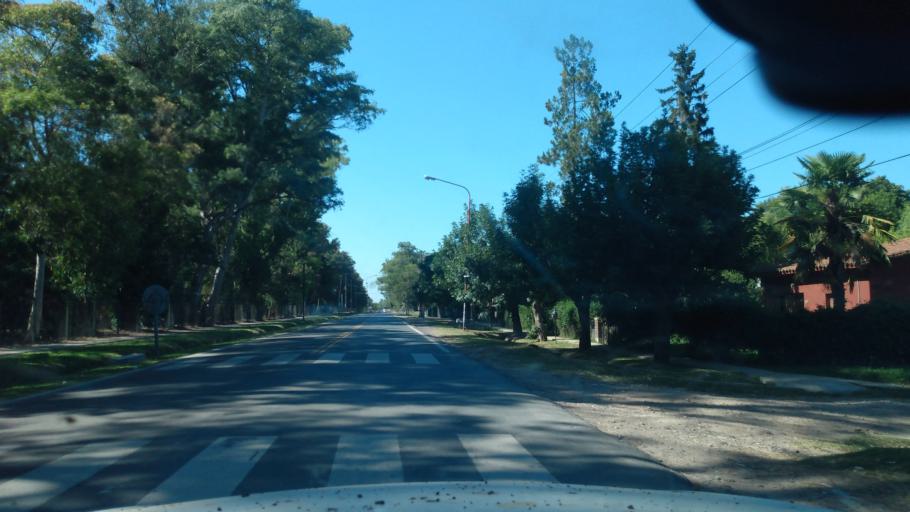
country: AR
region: Buenos Aires
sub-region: Partido de Lujan
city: Lujan
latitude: -34.5001
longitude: -59.0710
